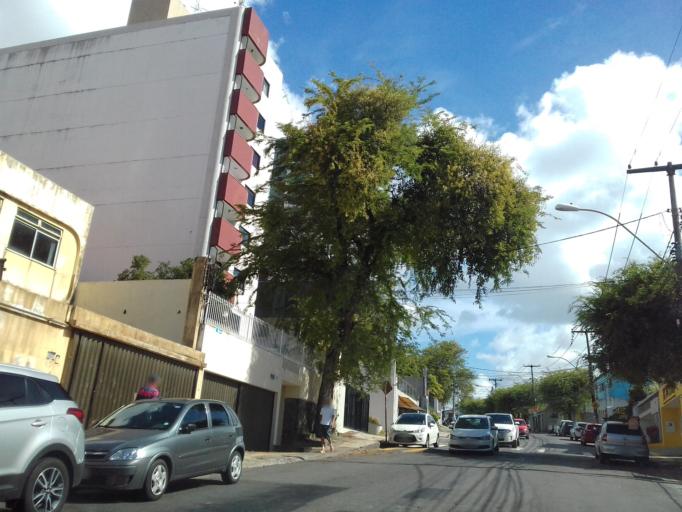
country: BR
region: Bahia
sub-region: Salvador
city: Salvador
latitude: -12.9849
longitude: -38.4608
